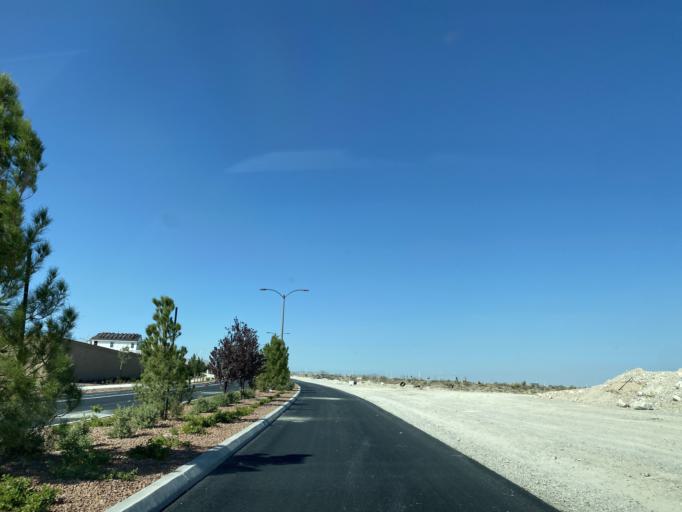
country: US
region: Nevada
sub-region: Clark County
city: Summerlin South
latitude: 36.3198
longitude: -115.3089
